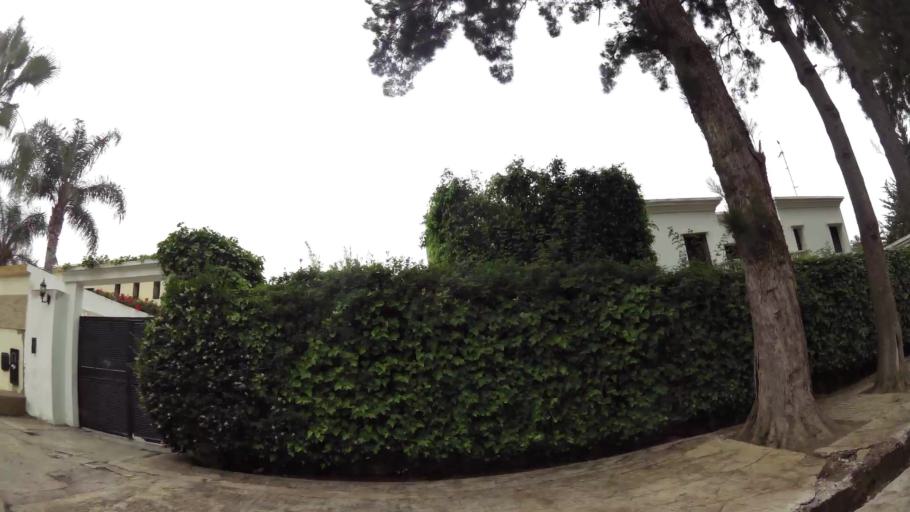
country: MA
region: Rabat-Sale-Zemmour-Zaer
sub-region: Rabat
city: Rabat
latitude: 33.9624
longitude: -6.8128
